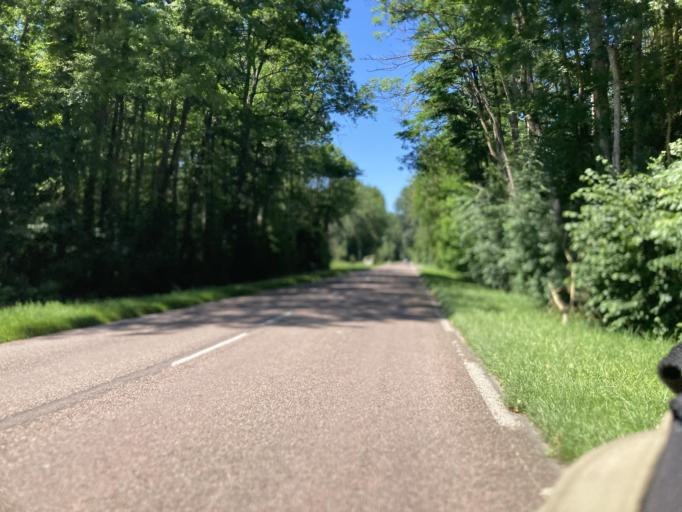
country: FR
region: Bourgogne
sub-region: Departement de l'Yonne
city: Laroche-Saint-Cydroine
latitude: 47.9655
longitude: 3.4650
